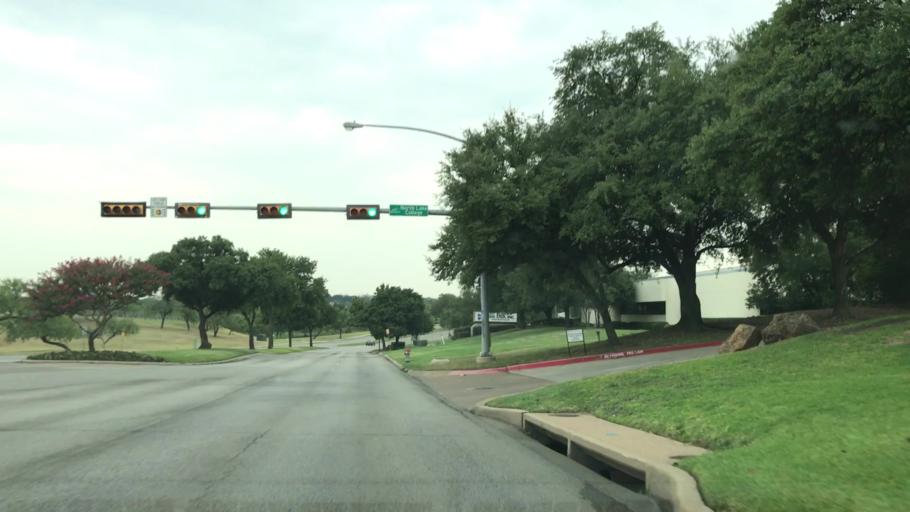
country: US
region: Texas
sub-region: Dallas County
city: Irving
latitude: 32.8719
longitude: -96.9710
